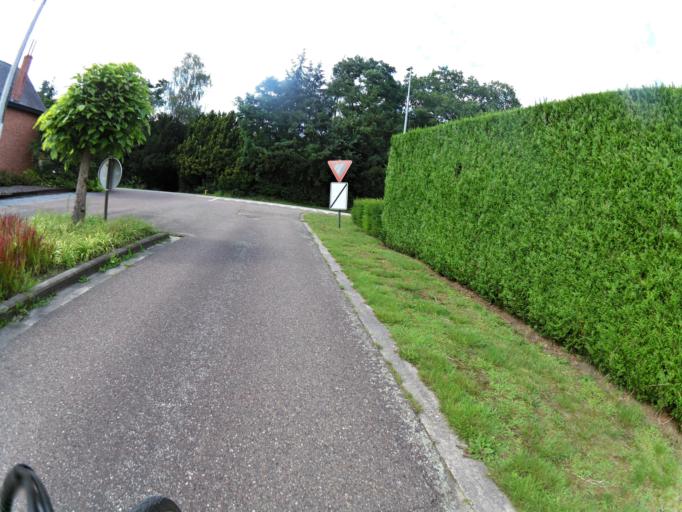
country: BE
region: Flanders
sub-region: Provincie Antwerpen
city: Balen
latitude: 51.1915
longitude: 5.2020
